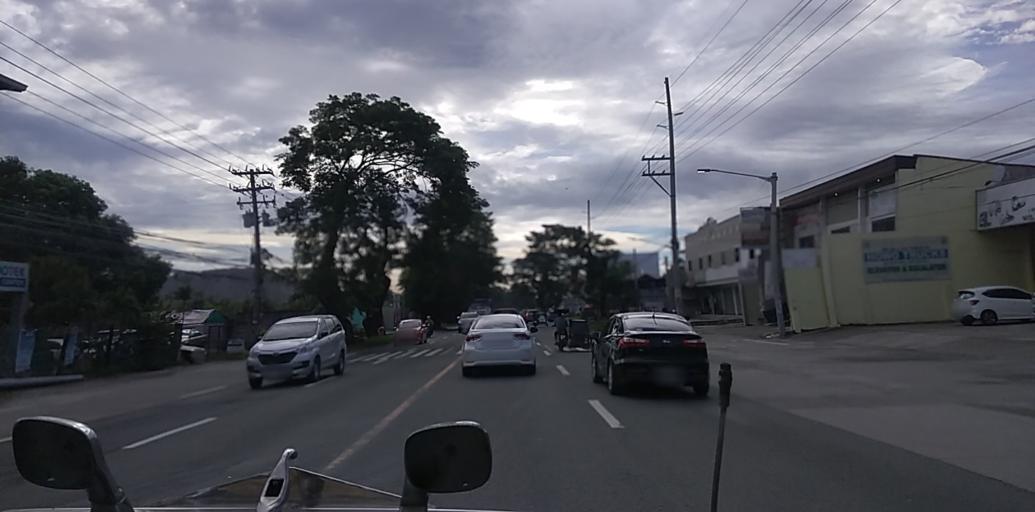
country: PH
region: Central Luzon
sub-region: Province of Pampanga
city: Telabastagan
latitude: 15.0993
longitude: 120.6219
